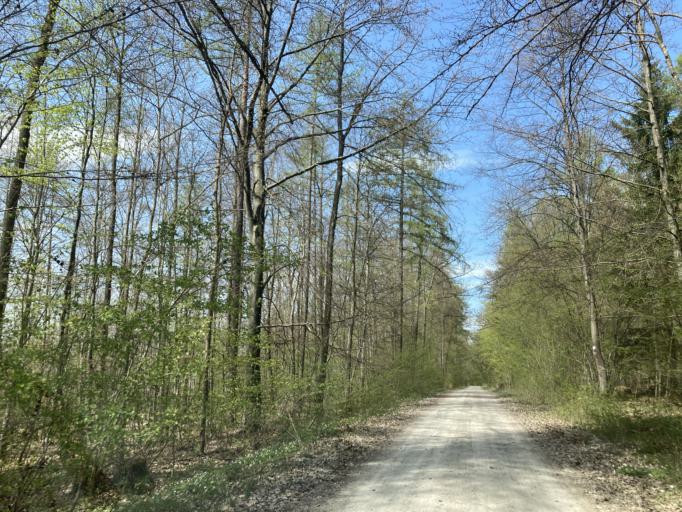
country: DE
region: Baden-Wuerttemberg
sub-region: Tuebingen Region
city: Bodelshausen
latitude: 48.4351
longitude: 8.9856
